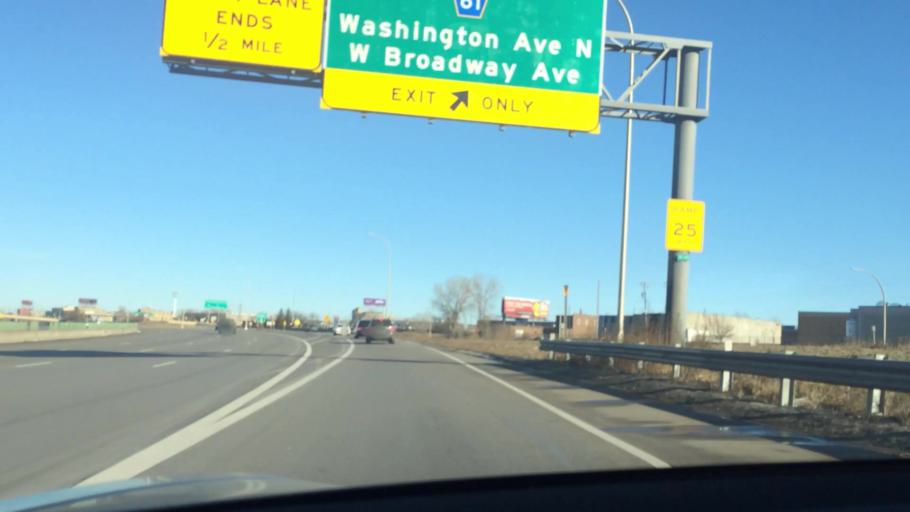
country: US
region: Minnesota
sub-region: Hennepin County
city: Minneapolis
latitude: 44.9927
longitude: -93.2840
